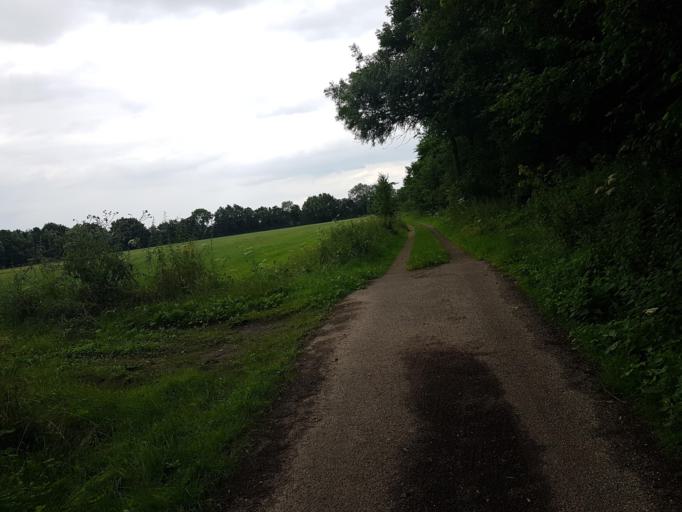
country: NL
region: Gelderland
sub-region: Gemeente Rheden
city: Ellecom
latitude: 52.0148
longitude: 6.0834
